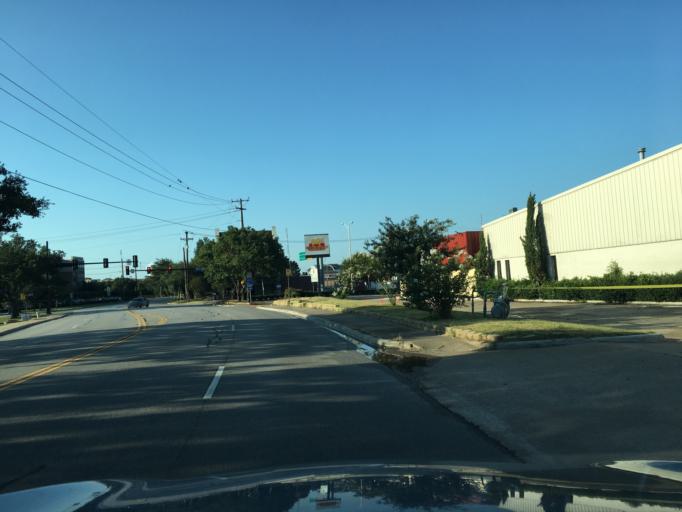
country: US
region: Texas
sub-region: Dallas County
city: Addison
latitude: 32.9695
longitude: -96.8304
